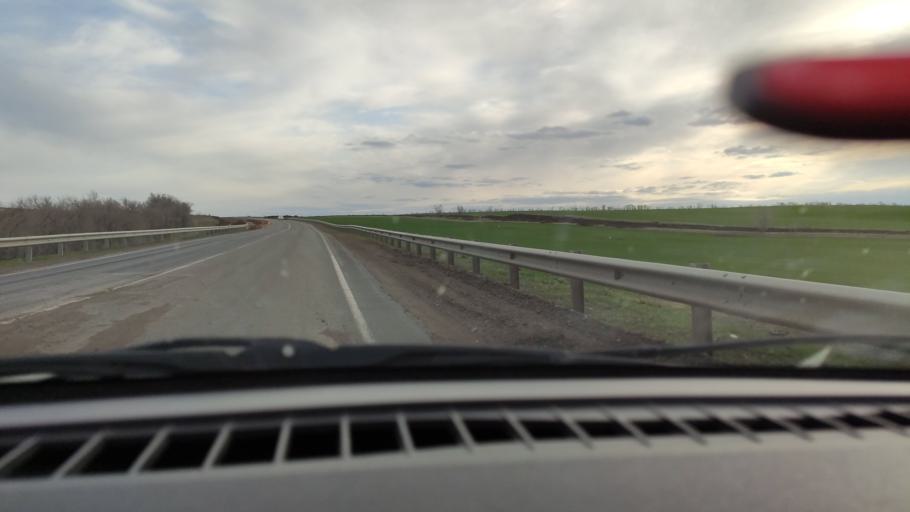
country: RU
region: Orenburg
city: Sakmara
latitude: 52.1867
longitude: 55.2962
